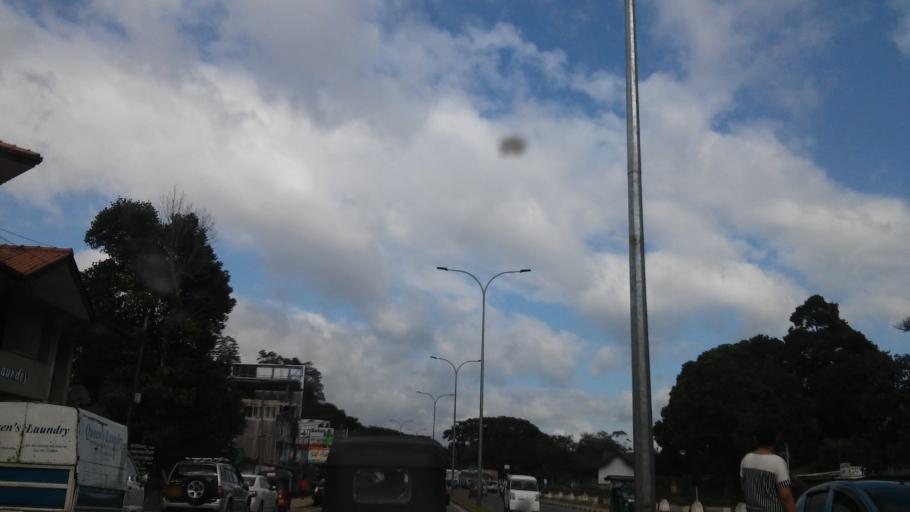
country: LK
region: Central
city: Kandy
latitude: 7.2721
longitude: 80.6084
